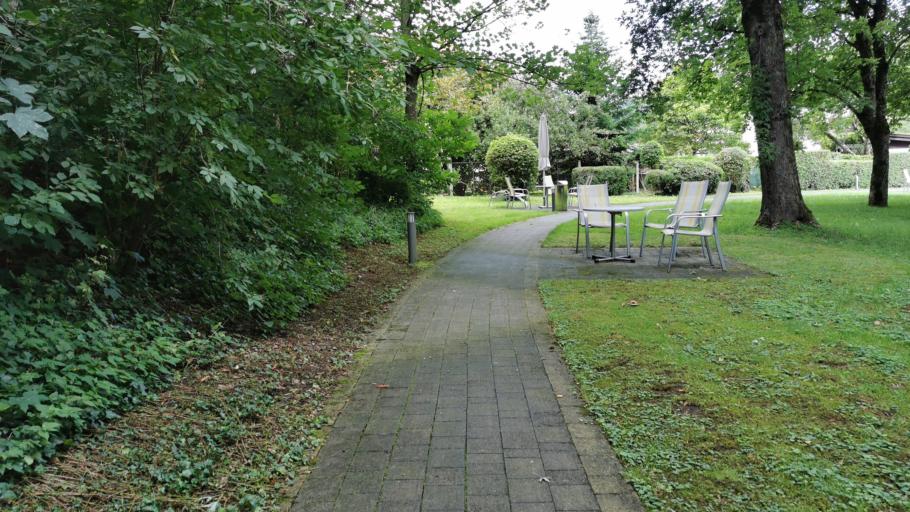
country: AT
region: Lower Austria
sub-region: Waidhofen an der Ybbs Stadt
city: Waidhofen an der Ybbs
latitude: 47.9524
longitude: 14.7865
